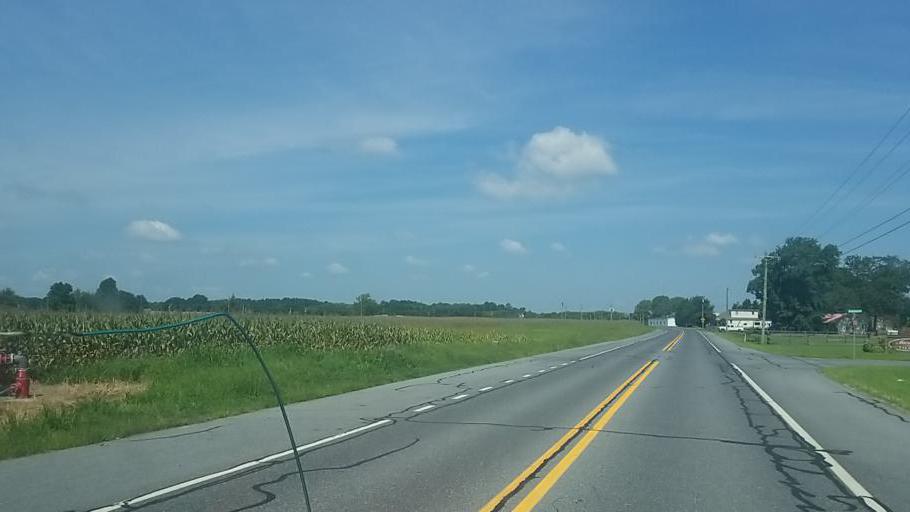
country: US
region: Delaware
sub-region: Sussex County
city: Seaford
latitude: 38.6824
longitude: -75.5860
